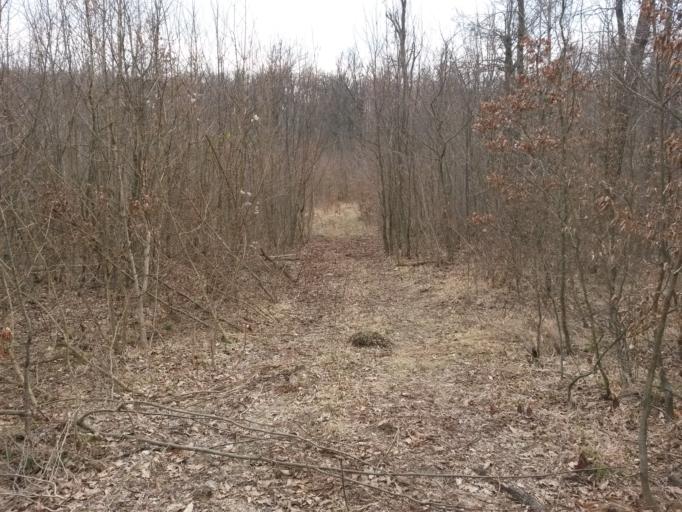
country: HU
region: Pest
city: Telki
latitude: 47.5865
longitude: 18.8464
